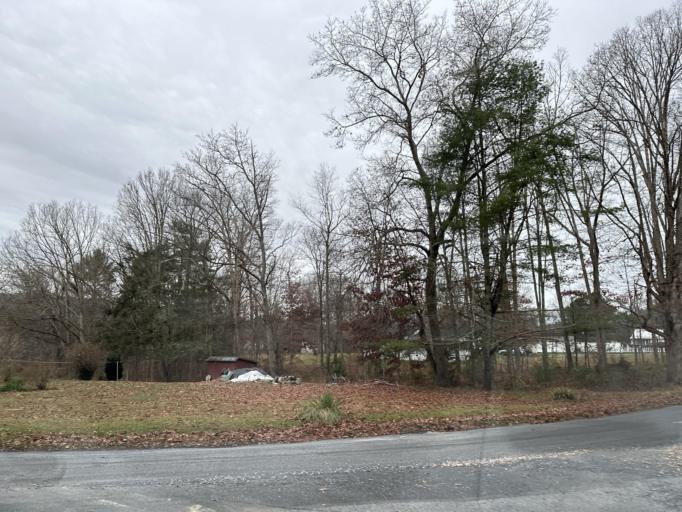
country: US
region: Virginia
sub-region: Rockbridge County
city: East Lexington
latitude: 38.0807
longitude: -79.3901
